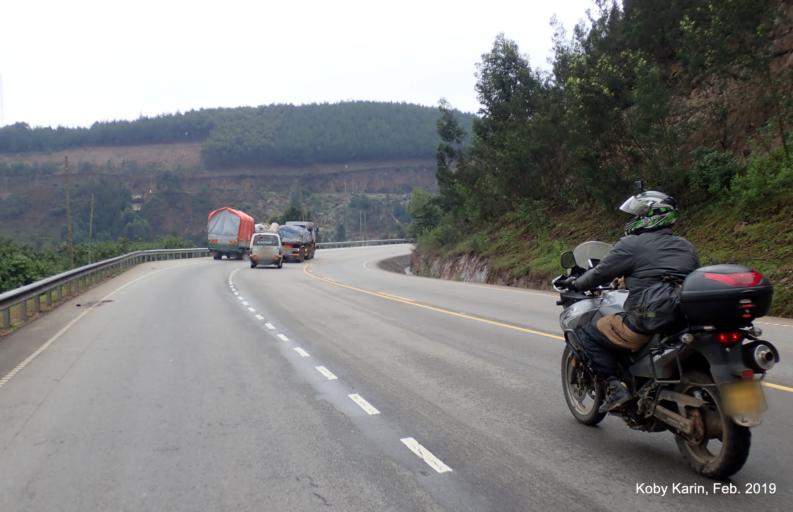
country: UG
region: Western Region
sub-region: Kabale District
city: Kabale
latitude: -1.2312
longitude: 30.0547
